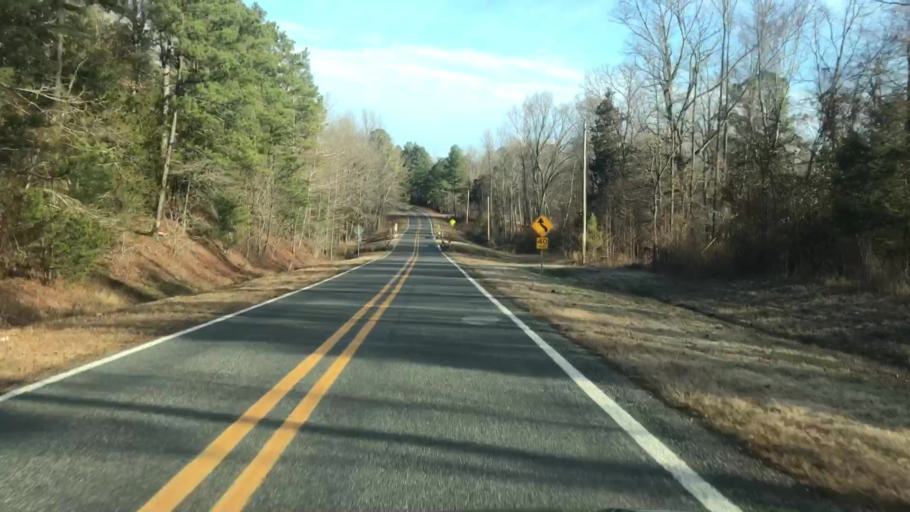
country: US
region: Arkansas
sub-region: Garland County
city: Rockwell
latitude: 34.4900
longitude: -93.2760
